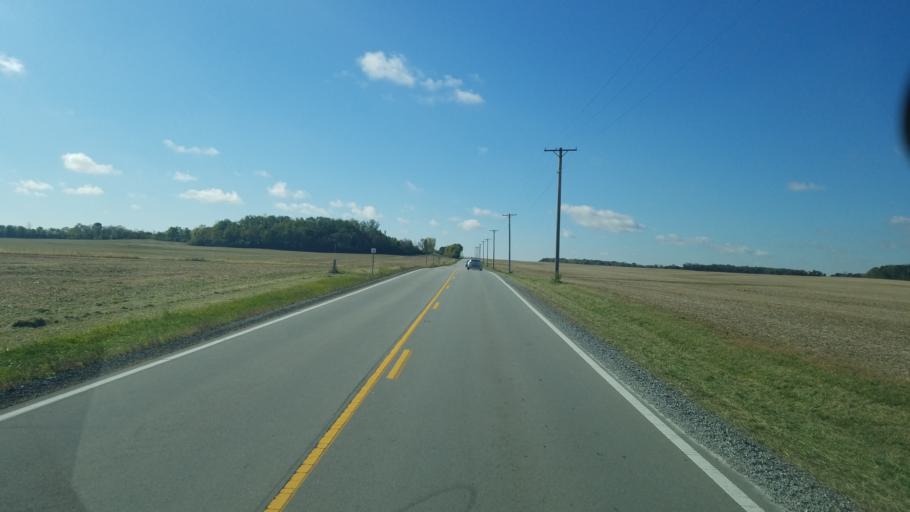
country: US
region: Ohio
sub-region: Highland County
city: Leesburg
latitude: 39.4310
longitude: -83.5137
